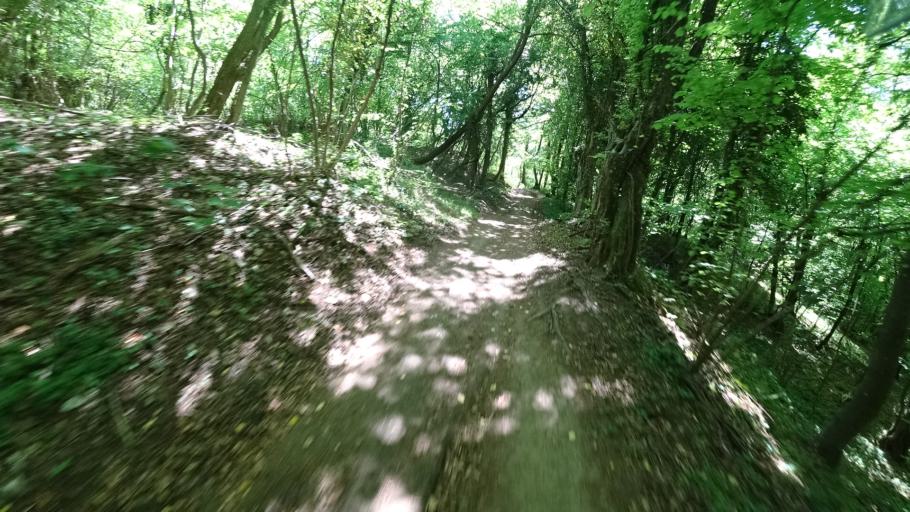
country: HR
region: Zagrebacka
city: Jablanovec
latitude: 45.8512
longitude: 15.8576
